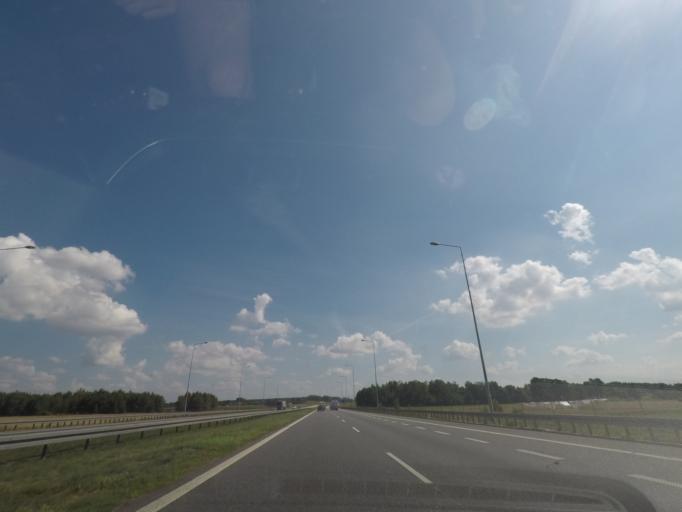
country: PL
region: Lodz Voivodeship
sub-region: Powiat zgierski
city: Strykow
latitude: 51.8774
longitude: 19.6478
